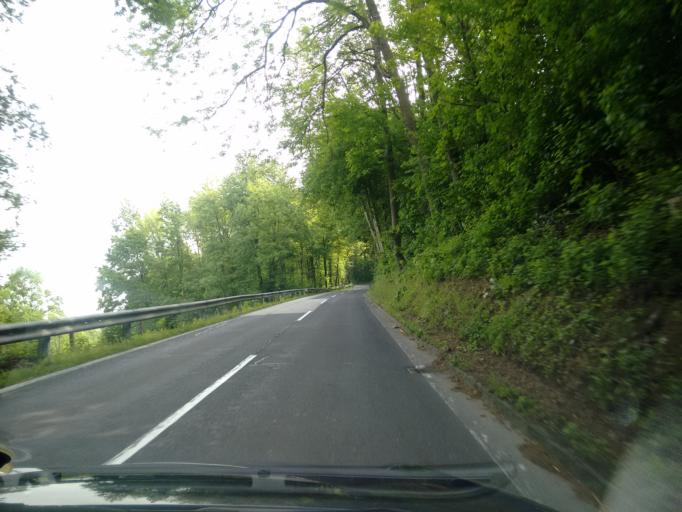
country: AT
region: Upper Austria
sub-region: Wels-Land
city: Thalheim bei Wels
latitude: 48.1535
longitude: 14.0508
